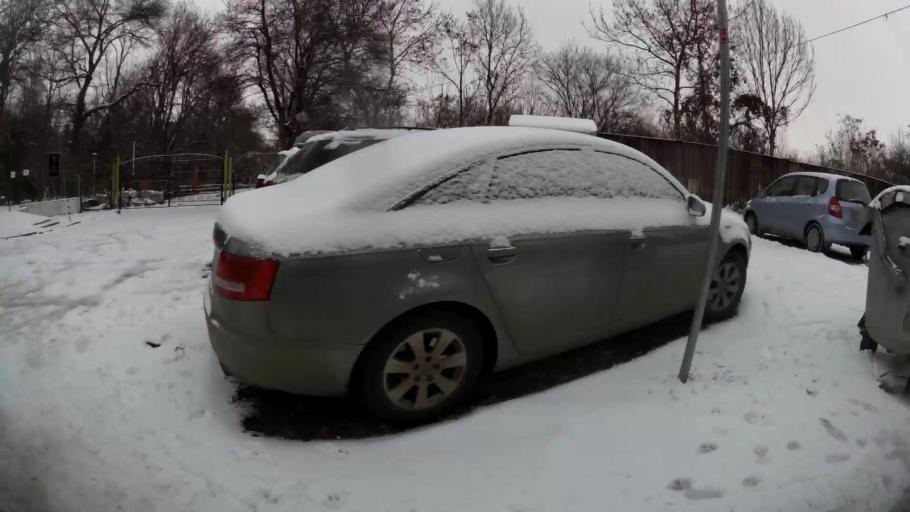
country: BG
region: Sofia-Capital
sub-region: Stolichna Obshtina
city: Sofia
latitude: 42.6890
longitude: 23.3474
